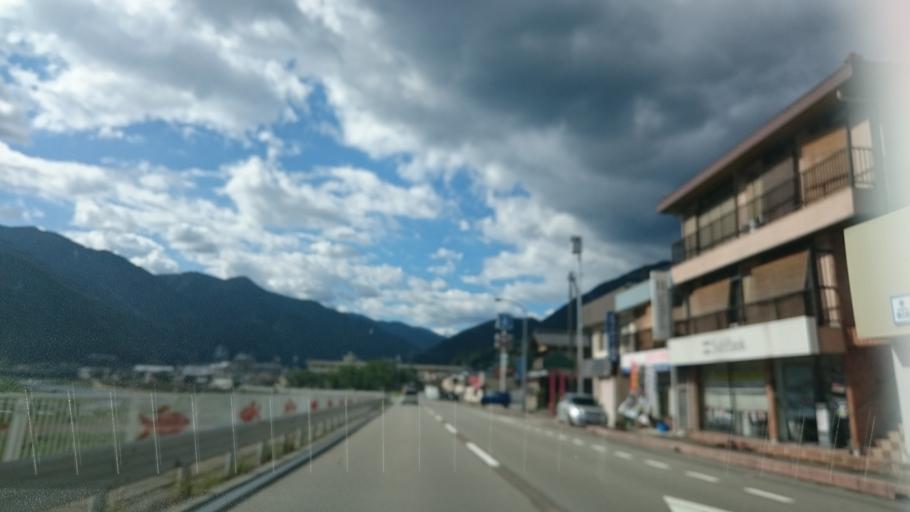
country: JP
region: Gifu
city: Gujo
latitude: 35.7972
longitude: 137.2544
